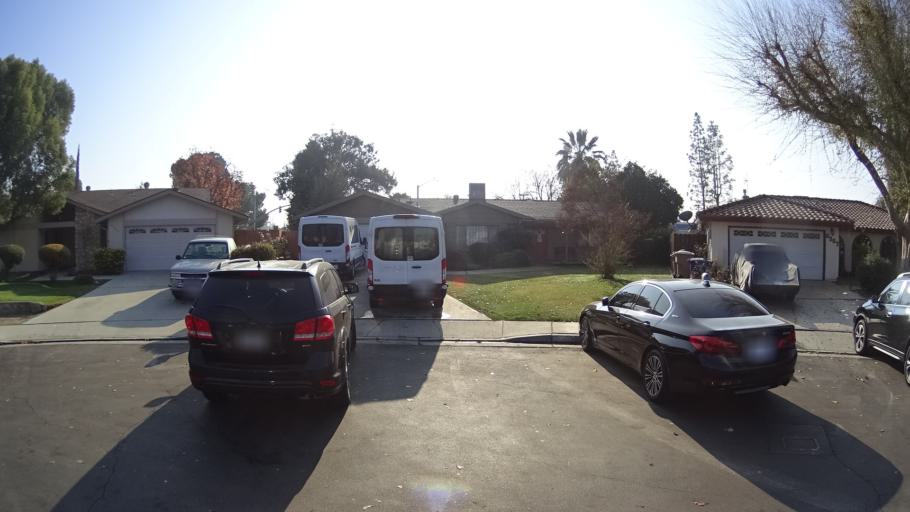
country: US
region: California
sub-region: Kern County
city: Greenacres
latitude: 35.3353
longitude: -119.0752
